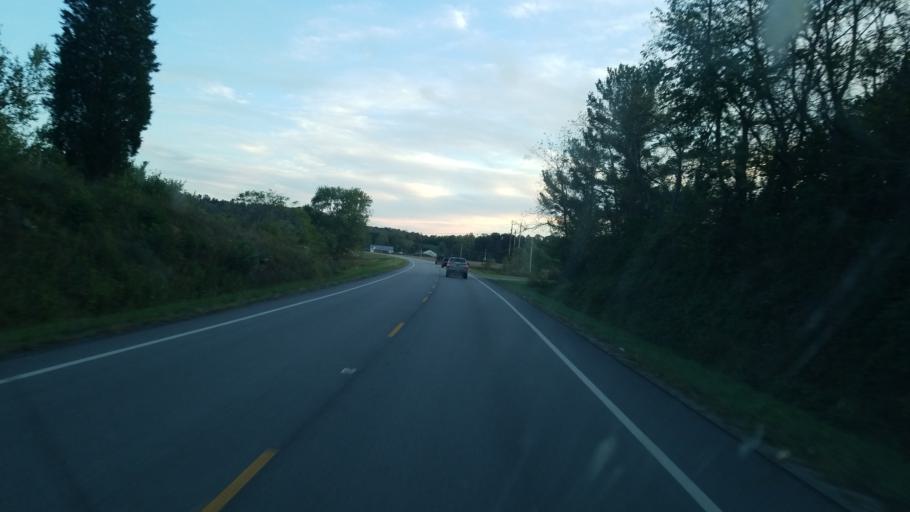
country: US
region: West Virginia
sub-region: Mason County
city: New Haven
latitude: 39.0957
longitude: -81.9271
